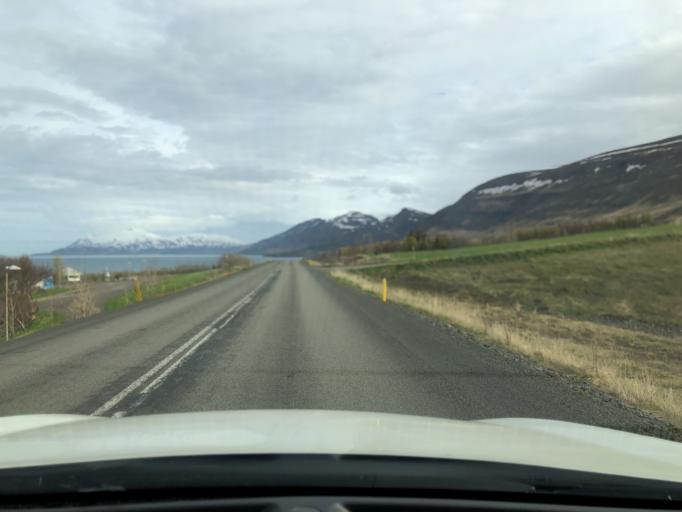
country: IS
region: Northeast
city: Akureyri
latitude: 65.7715
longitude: -18.0703
